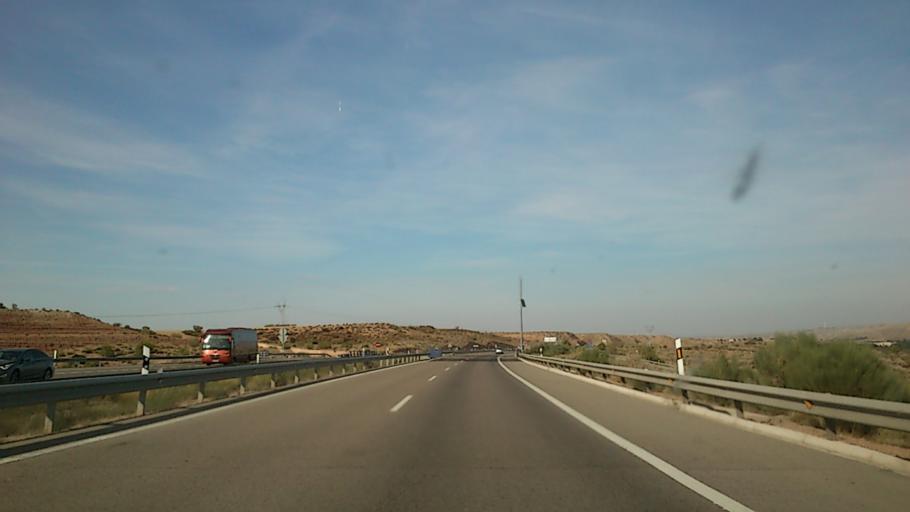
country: ES
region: Aragon
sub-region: Provincia de Zaragoza
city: Botorrita
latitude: 41.5166
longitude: -1.0370
